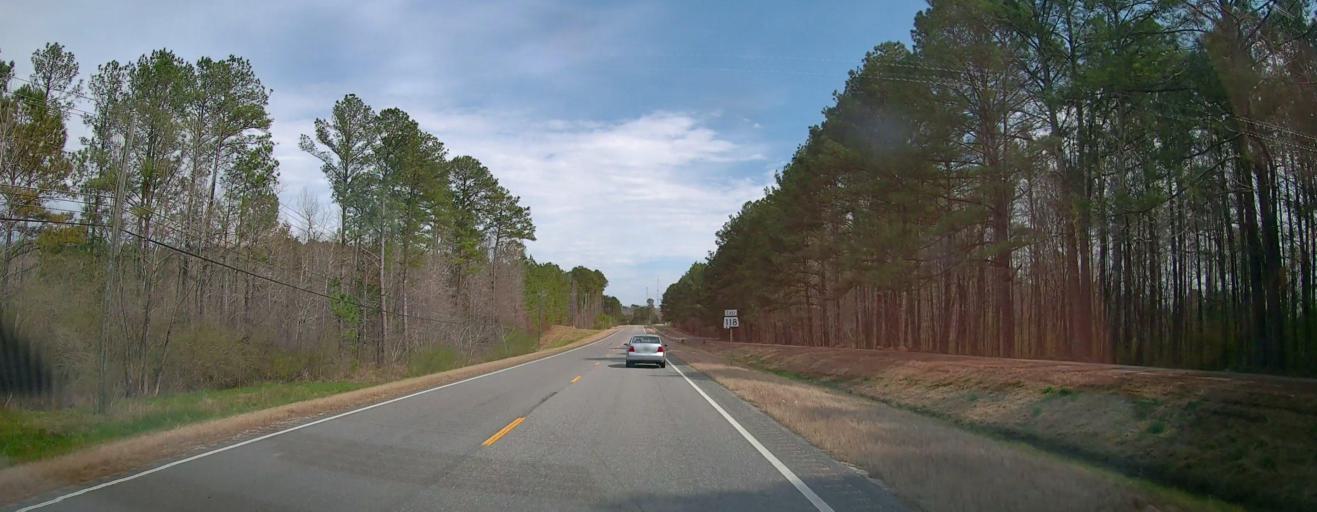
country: US
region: Alabama
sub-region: Walker County
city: Carbon Hill
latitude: 33.9217
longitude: -87.5850
